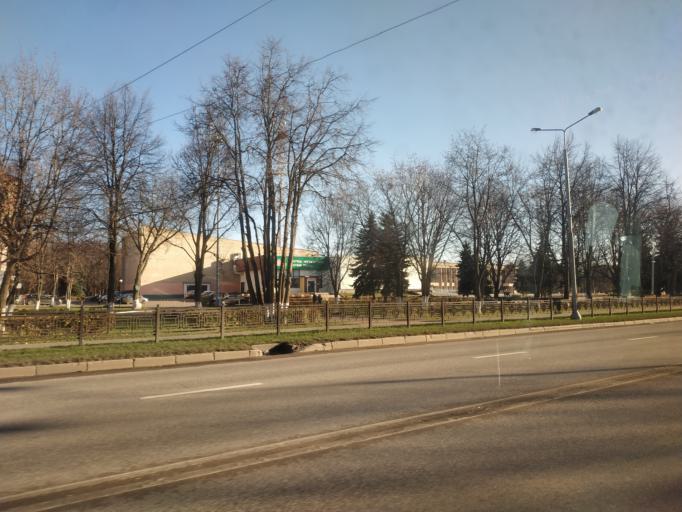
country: RU
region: Moskovskaya
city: Domodedovo
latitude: 55.4384
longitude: 37.7664
